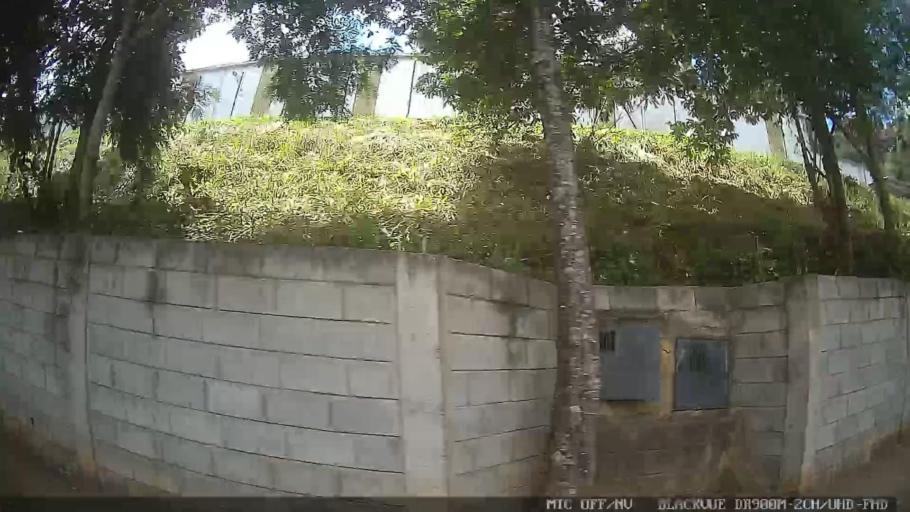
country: BR
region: Minas Gerais
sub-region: Extrema
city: Extrema
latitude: -22.8521
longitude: -46.3044
